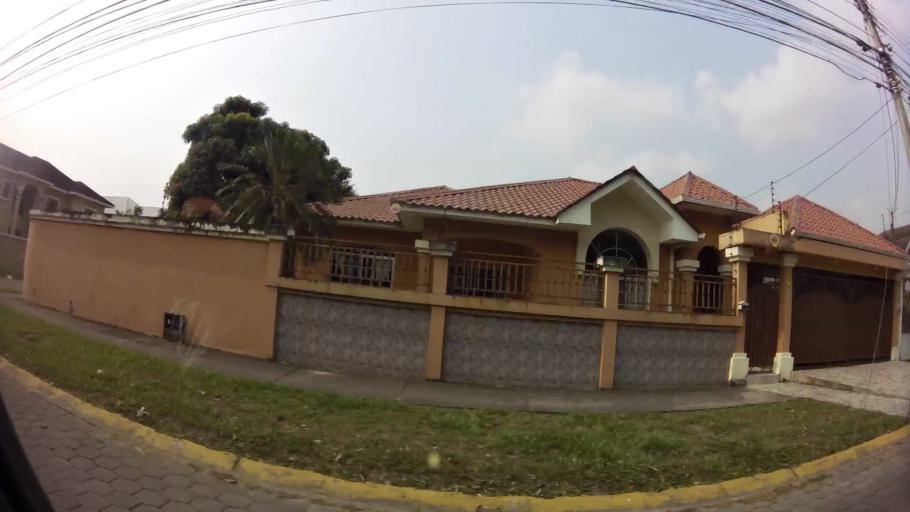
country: HN
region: Cortes
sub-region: San Pedro Sula
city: Pena Blanca
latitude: 15.5380
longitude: -88.0293
